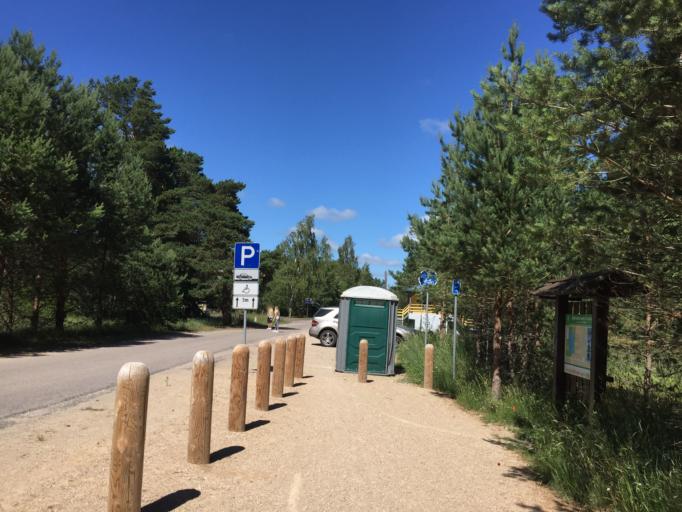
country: LV
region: Ventspils
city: Ventspils
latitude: 57.4527
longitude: 21.6288
